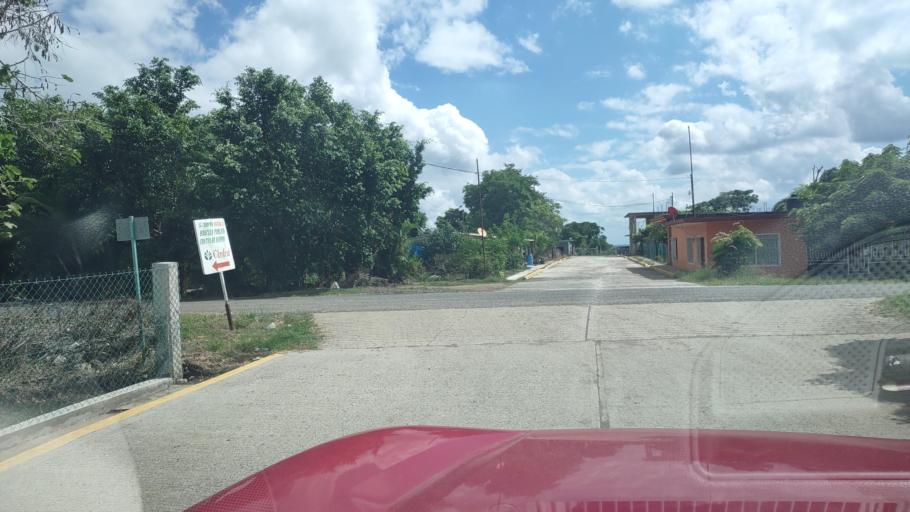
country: MX
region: Puebla
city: San Jose Acateno
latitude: 20.2737
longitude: -97.1302
